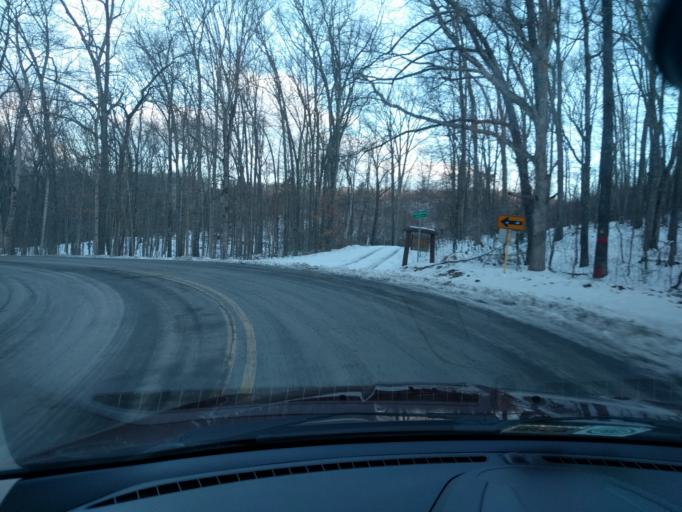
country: US
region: Virginia
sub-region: Bath County
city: Warm Springs
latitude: 38.0983
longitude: -79.8478
